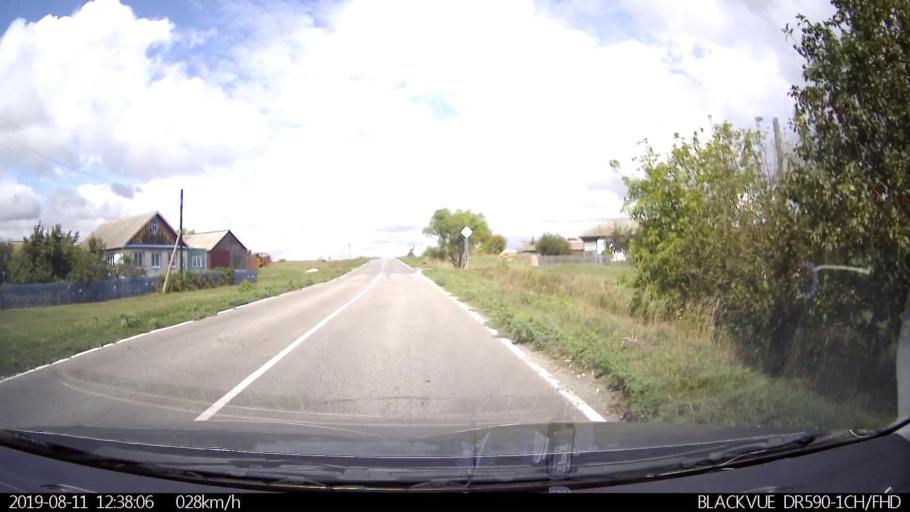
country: RU
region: Ulyanovsk
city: Ignatovka
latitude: 53.8250
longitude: 47.8086
